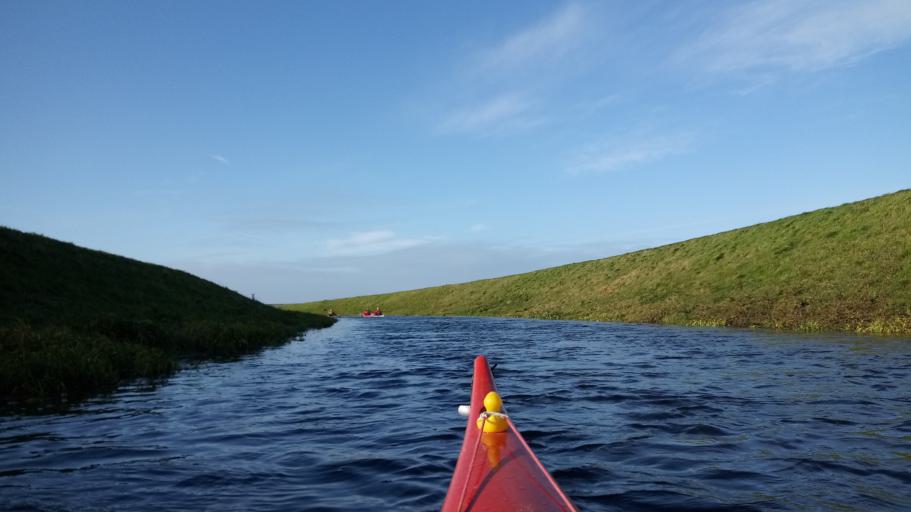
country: NL
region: Gelderland
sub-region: Gemeente Bronckhorst
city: Baak
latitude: 52.1001
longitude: 6.2240
